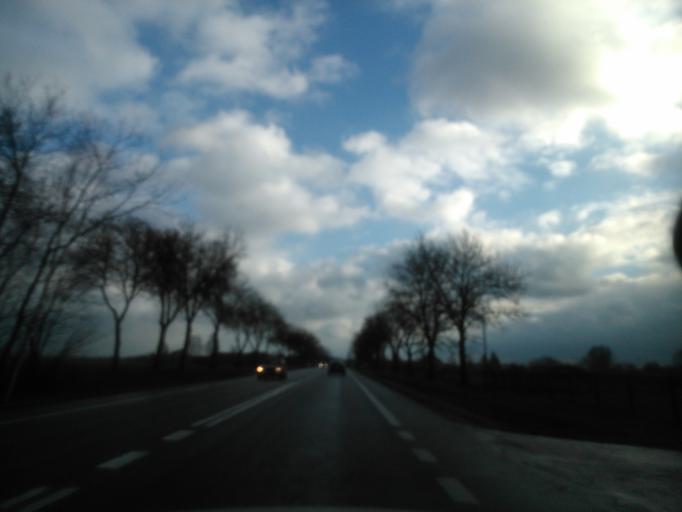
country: PL
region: Masovian Voivodeship
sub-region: Powiat sierpecki
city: Rosciszewo
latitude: 52.8311
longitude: 19.7507
